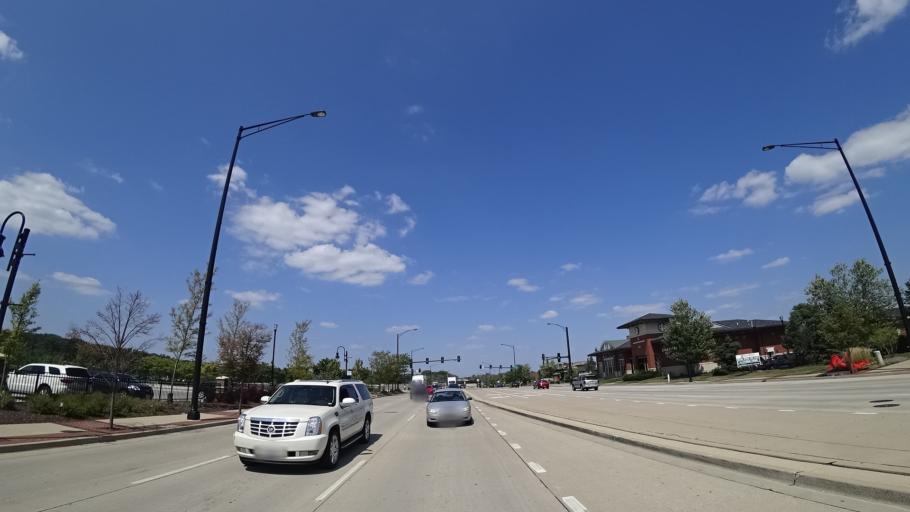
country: US
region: Illinois
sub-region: Cook County
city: Orland Park
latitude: 41.6315
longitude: -87.8540
